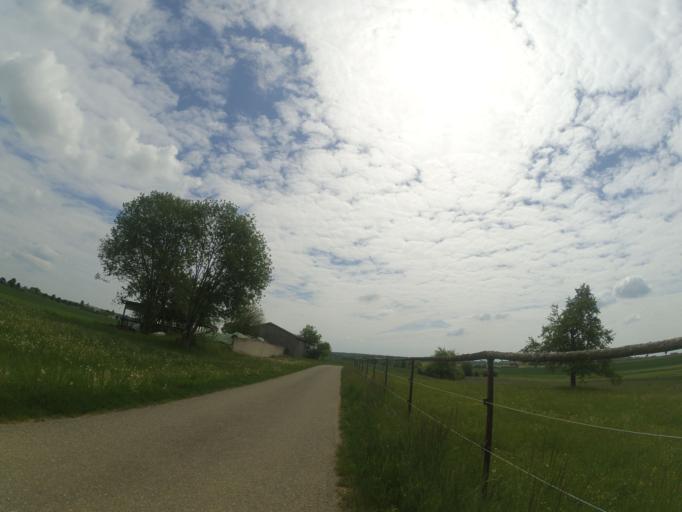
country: DE
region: Baden-Wuerttemberg
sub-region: Tuebingen Region
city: Berghulen
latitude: 48.4580
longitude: 9.7645
